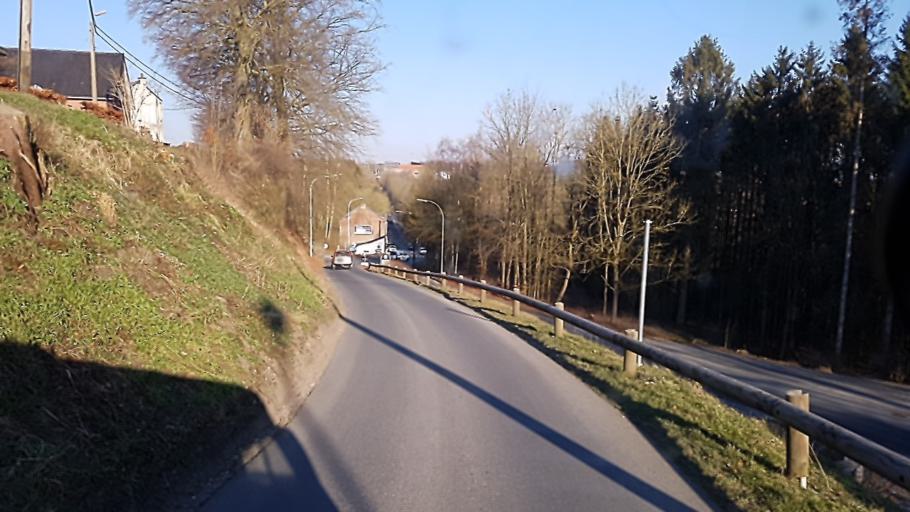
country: BE
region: Wallonia
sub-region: Province du Hainaut
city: Beaumont
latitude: 50.2381
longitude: 4.2387
